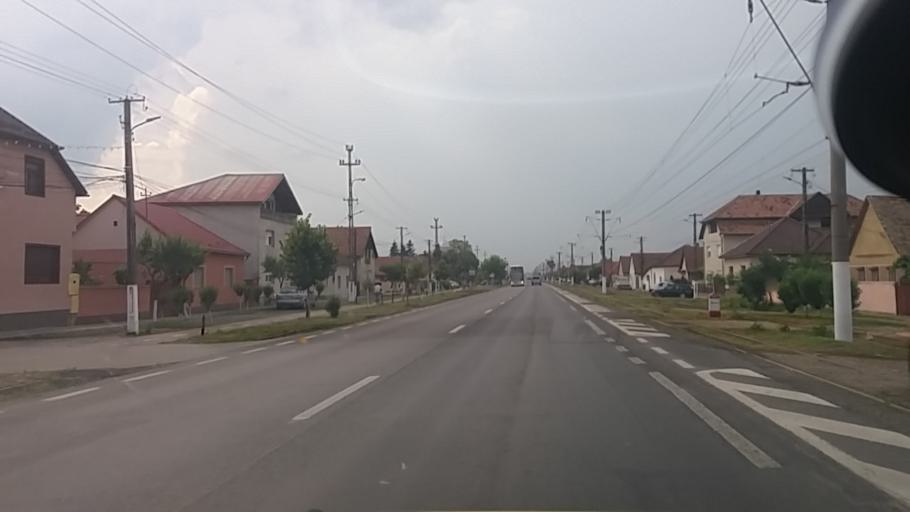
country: RO
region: Arad
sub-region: Comuna Vladimirescu
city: Vladimirescu
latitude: 46.1645
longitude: 21.4018
